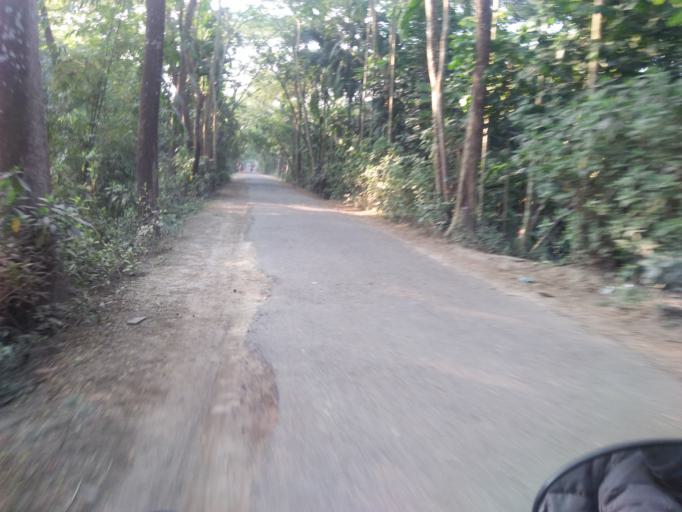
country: BD
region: Barisal
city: Bhola
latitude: 22.7532
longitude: 90.6295
